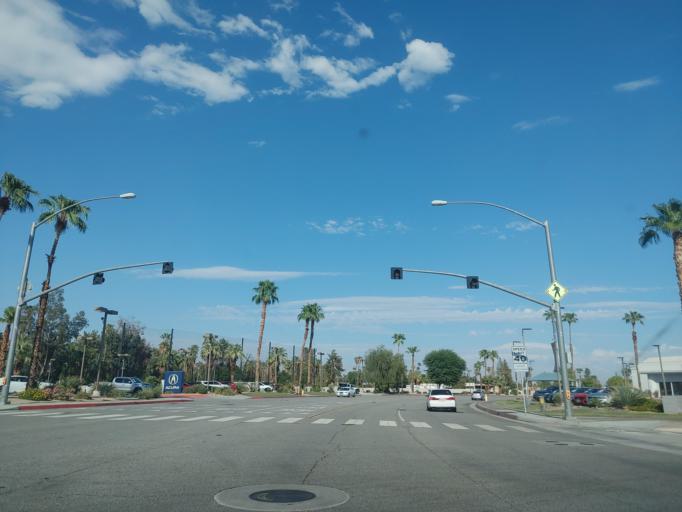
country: US
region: California
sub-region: Riverside County
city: Cathedral City
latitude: 33.7858
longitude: -116.4743
